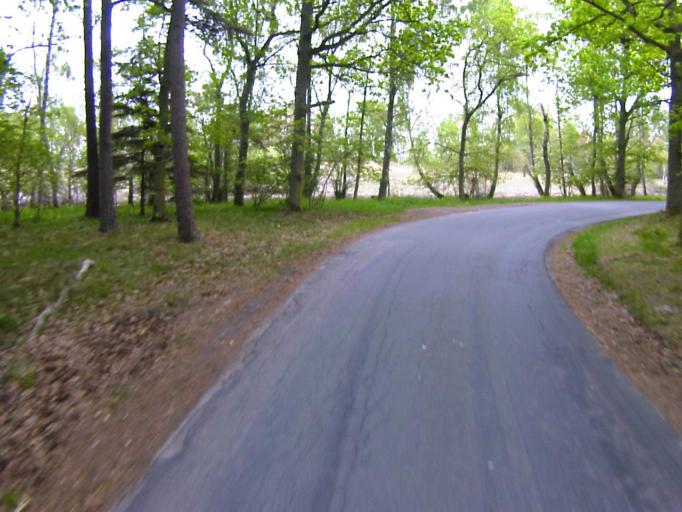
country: SE
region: Skane
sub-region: Kristianstads Kommun
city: Ahus
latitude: 55.9210
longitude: 14.3191
